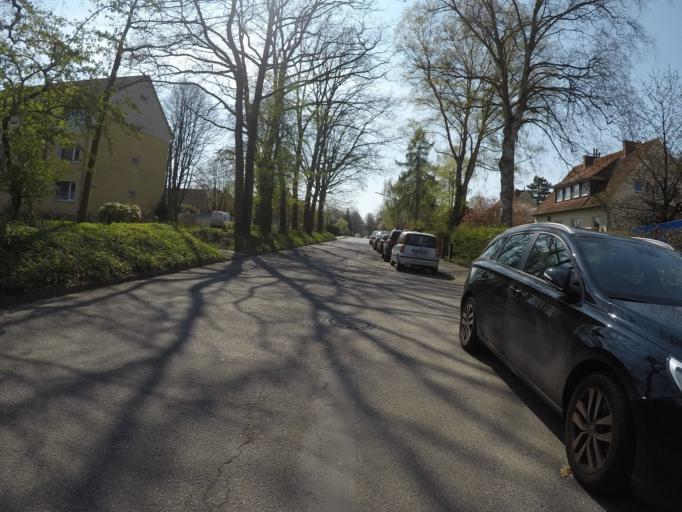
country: DE
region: Schleswig-Holstein
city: Halstenbek
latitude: 53.5833
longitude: 9.8171
